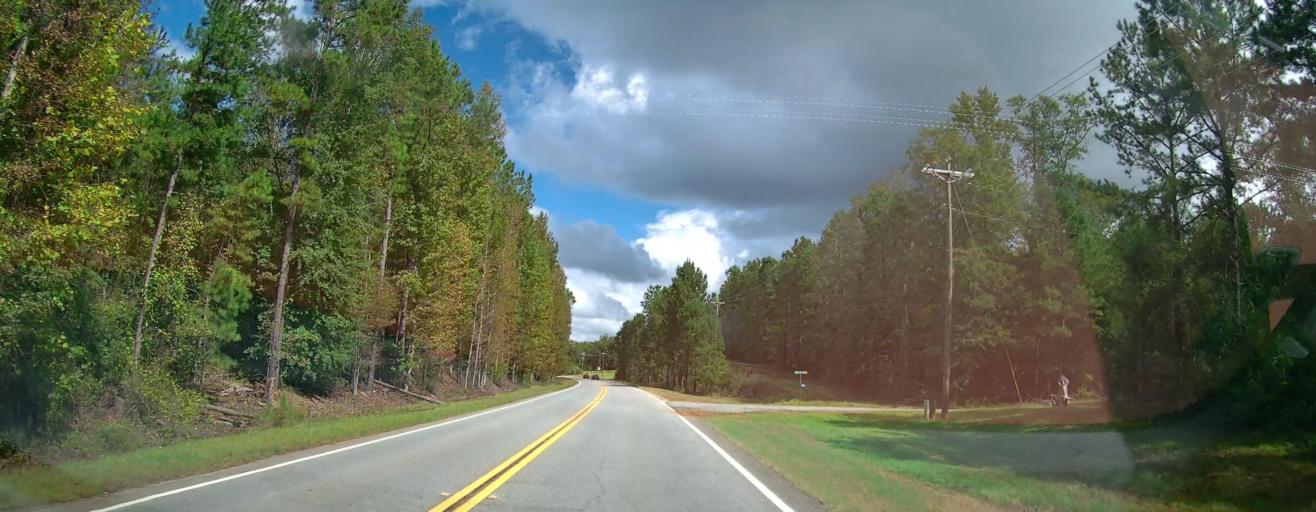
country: US
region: Georgia
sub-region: Jones County
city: Gray
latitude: 32.9634
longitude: -83.4327
